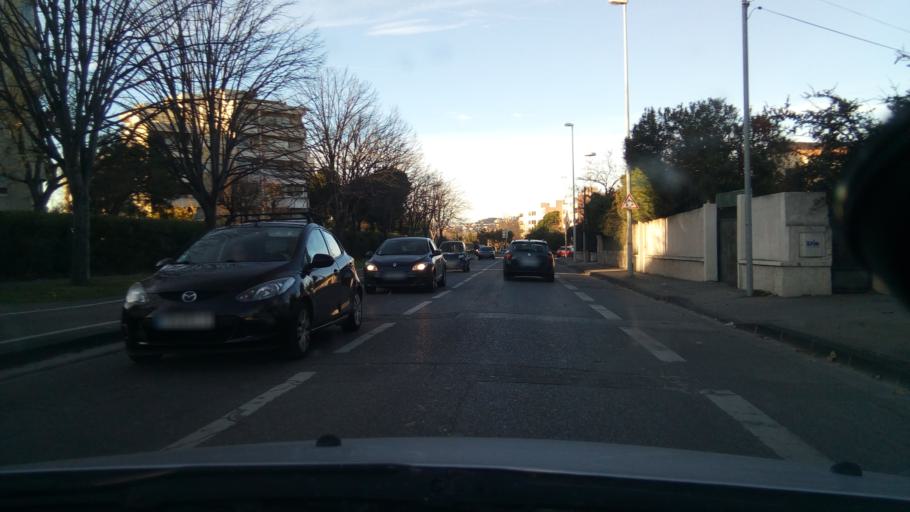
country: FR
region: Provence-Alpes-Cote d'Azur
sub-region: Departement des Bouches-du-Rhone
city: Marseille 09
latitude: 43.2449
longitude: 5.3960
